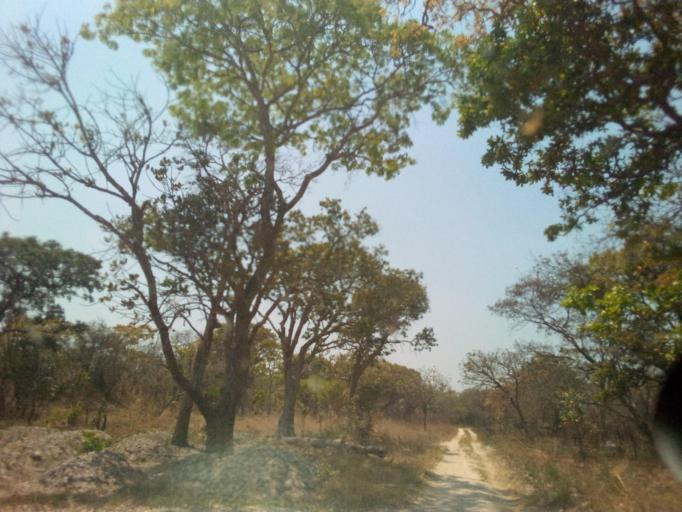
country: ZM
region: Copperbelt
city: Kataba
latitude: -12.2384
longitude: 30.4047
